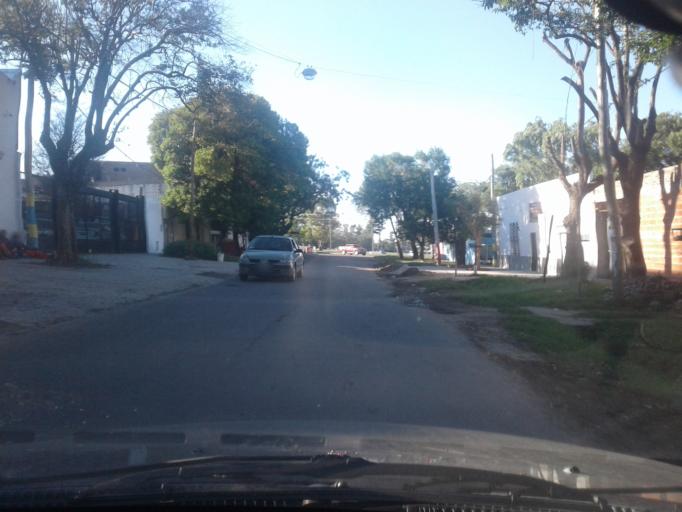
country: AR
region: Santa Fe
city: Granadero Baigorria
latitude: -32.8893
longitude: -60.7241
